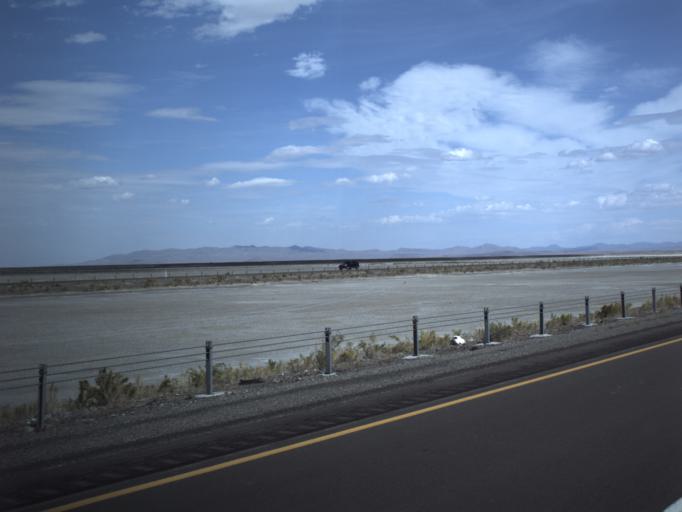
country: US
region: Utah
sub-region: Tooele County
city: Wendover
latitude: 40.7278
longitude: -113.3574
